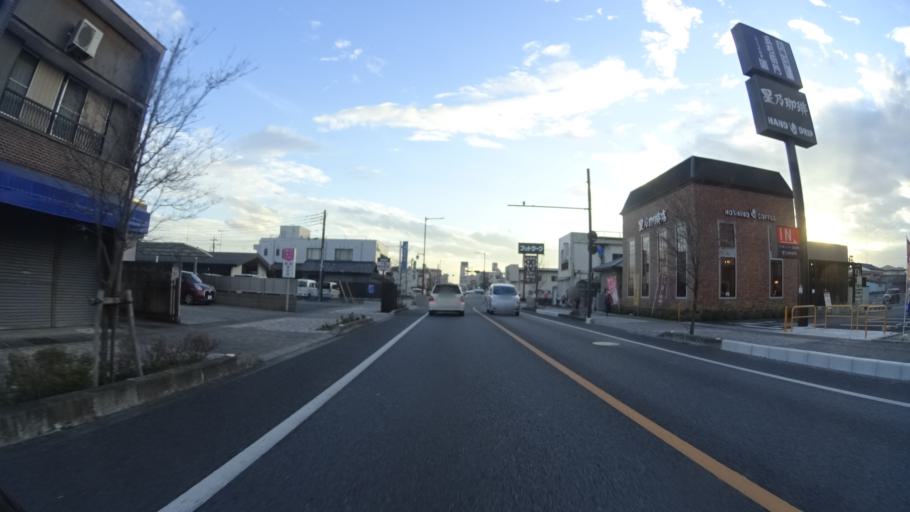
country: JP
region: Tochigi
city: Tochigi
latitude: 36.3879
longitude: 139.7357
